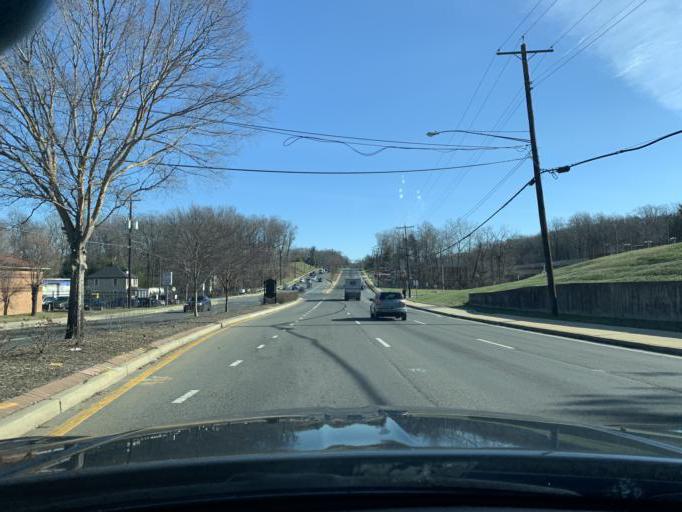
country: US
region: Maryland
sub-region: Prince George's County
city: Peppermill Village
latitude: 38.8872
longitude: -76.8946
